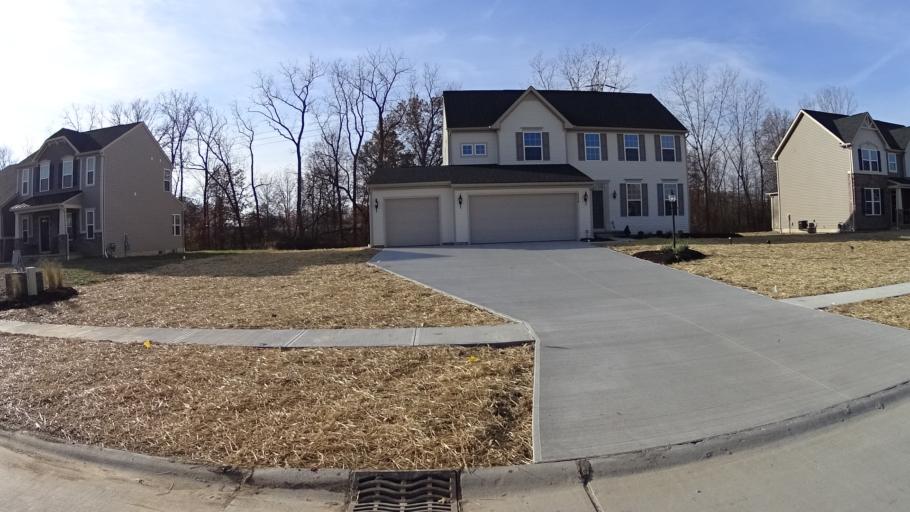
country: US
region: Ohio
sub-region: Lorain County
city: Avon
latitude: 41.4514
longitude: -82.0661
